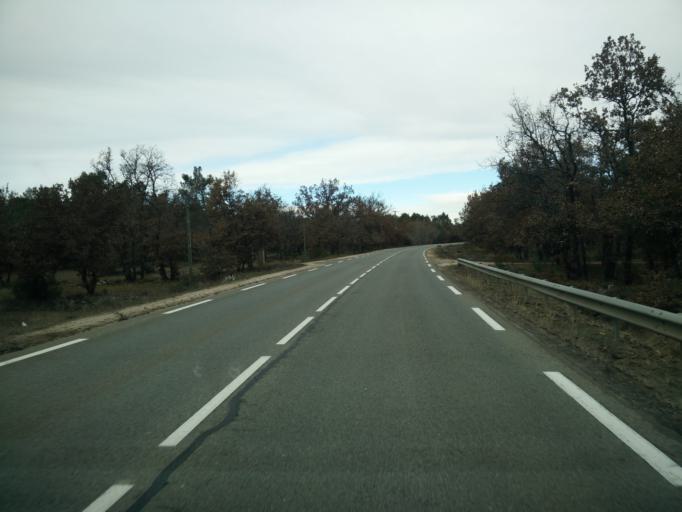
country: FR
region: Provence-Alpes-Cote d'Azur
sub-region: Departement du Var
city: Camps-la-Source
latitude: 43.3690
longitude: 6.0906
